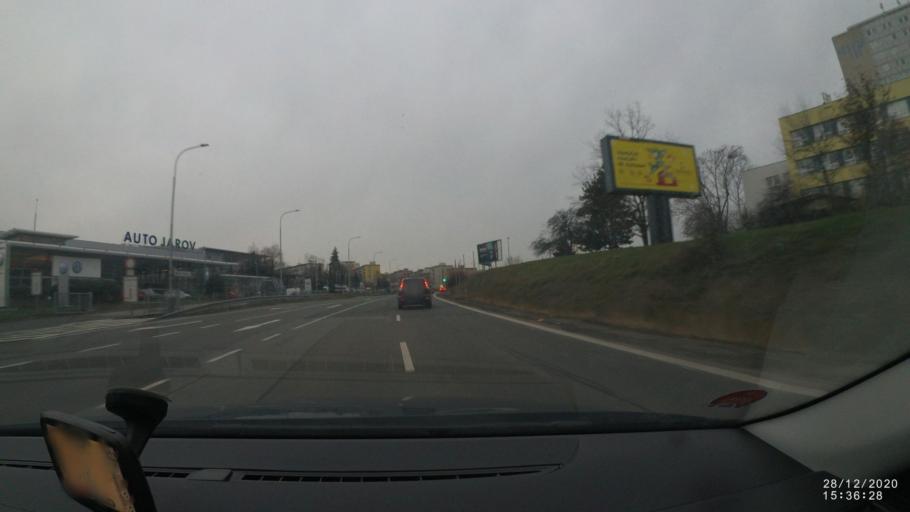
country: CZ
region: Praha
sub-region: Praha 9
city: Vysocany
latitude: 50.0907
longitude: 14.5013
